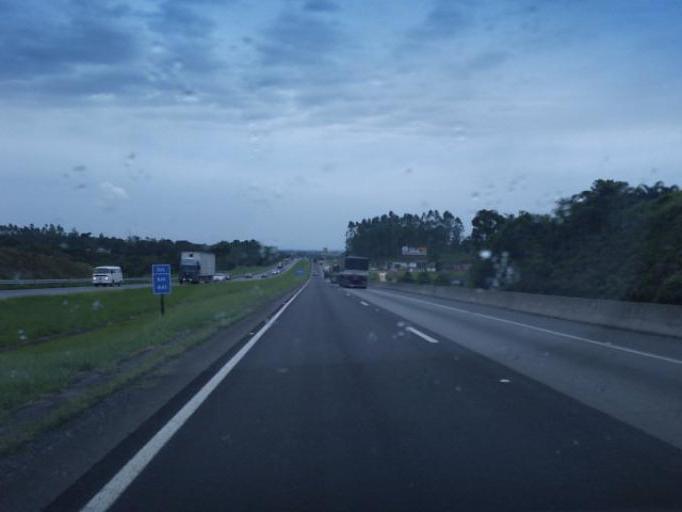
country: BR
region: Sao Paulo
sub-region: Registro
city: Registro
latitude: -24.4680
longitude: -47.8219
